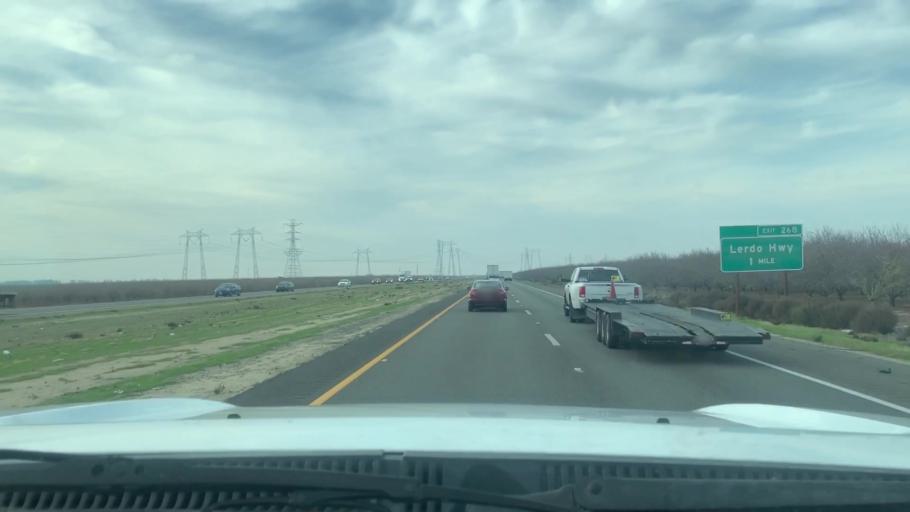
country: US
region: California
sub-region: Kern County
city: Buttonwillow
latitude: 35.4870
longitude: -119.5182
